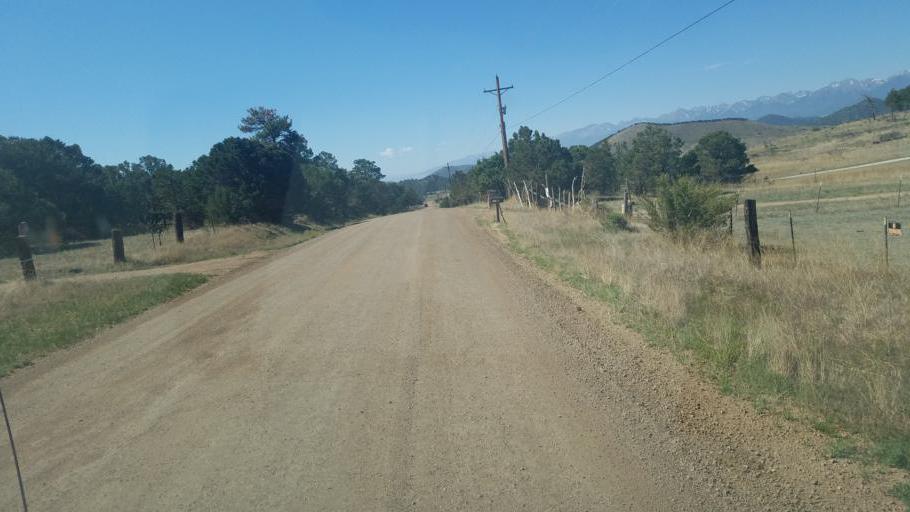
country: US
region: Colorado
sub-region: Custer County
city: Westcliffe
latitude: 38.3200
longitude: -105.4874
